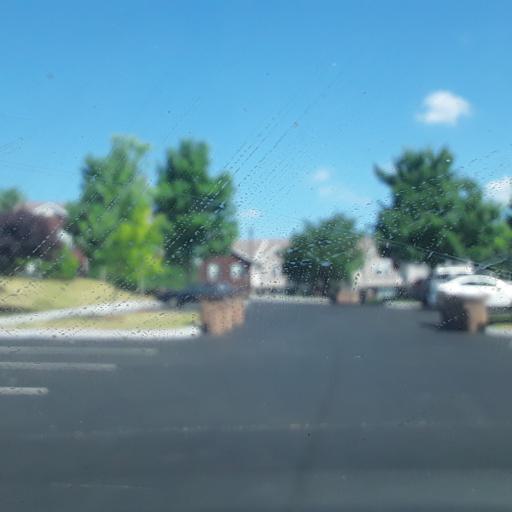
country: US
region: Tennessee
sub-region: Williamson County
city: Brentwood Estates
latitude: 36.0333
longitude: -86.7041
